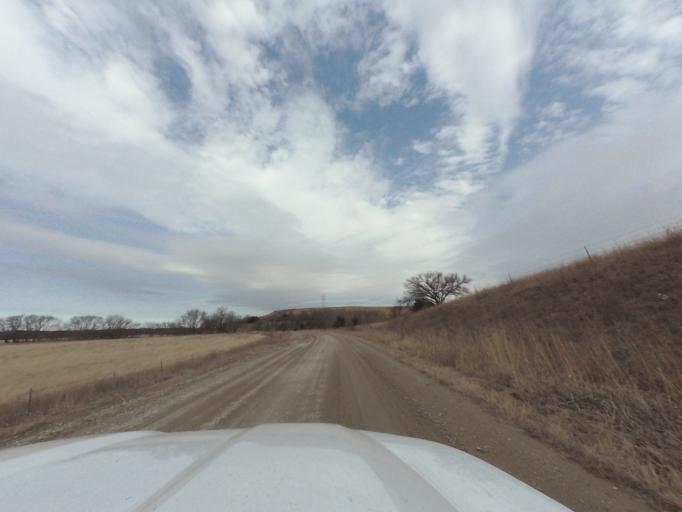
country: US
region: Kansas
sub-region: Chase County
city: Cottonwood Falls
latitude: 38.2771
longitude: -96.7338
